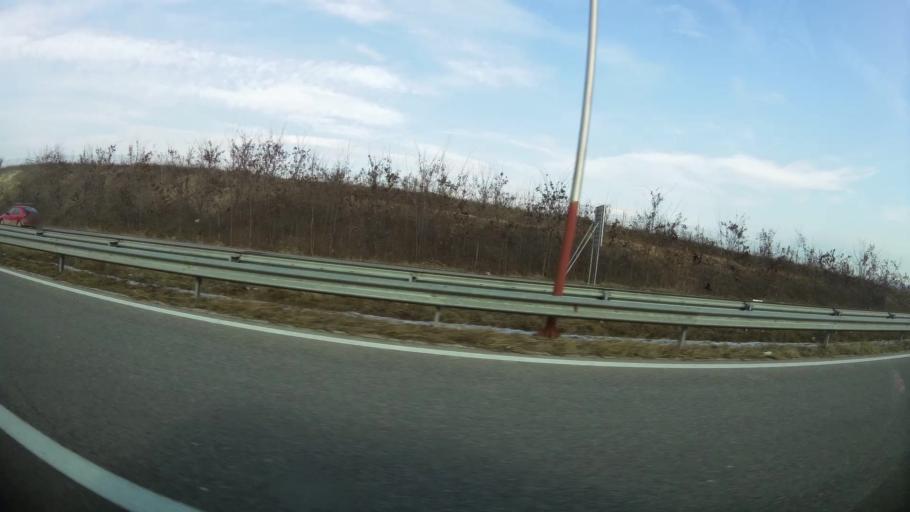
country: MK
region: Suto Orizari
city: Suto Orizare
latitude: 42.0484
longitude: 21.4350
